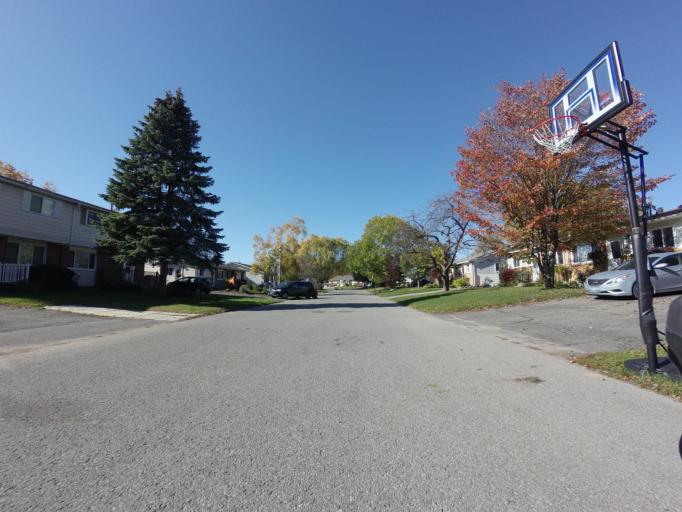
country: CA
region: Ontario
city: Bells Corners
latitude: 45.2910
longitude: -75.8740
